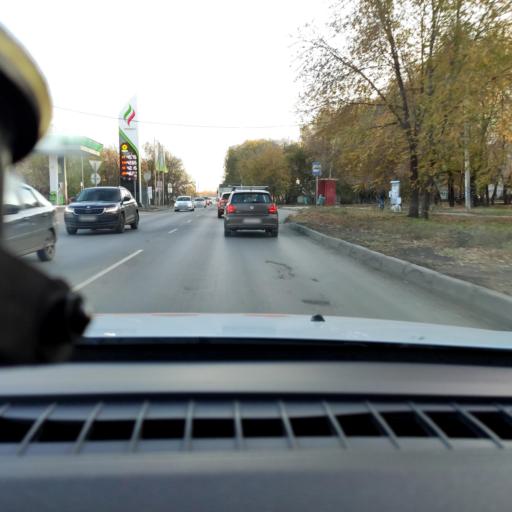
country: RU
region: Samara
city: Petra-Dubrava
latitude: 53.2476
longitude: 50.2689
